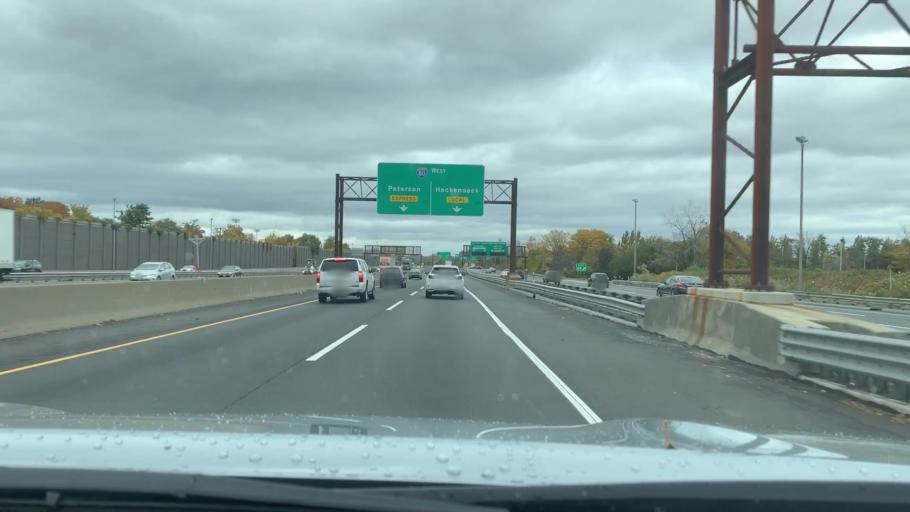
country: US
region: New Jersey
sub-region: Bergen County
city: Ridgefield Park
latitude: 40.8523
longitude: -74.0150
